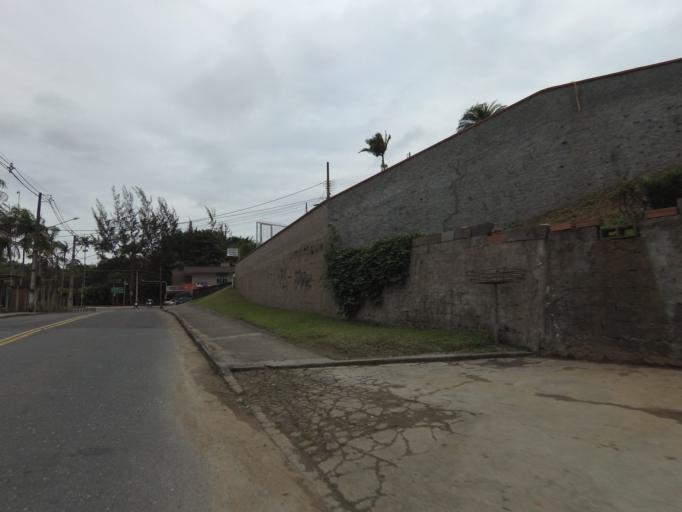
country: BR
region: Santa Catarina
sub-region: Blumenau
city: Blumenau
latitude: -26.8943
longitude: -49.1280
